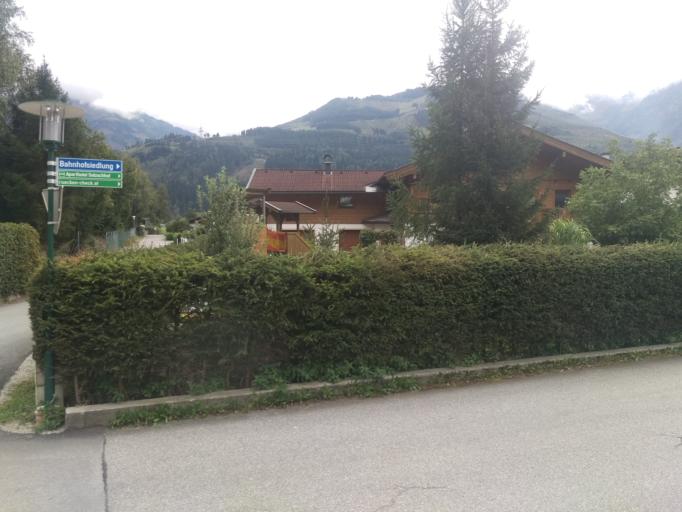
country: AT
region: Salzburg
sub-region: Politischer Bezirk Zell am See
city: Piesendorf
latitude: 47.2908
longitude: 12.7245
